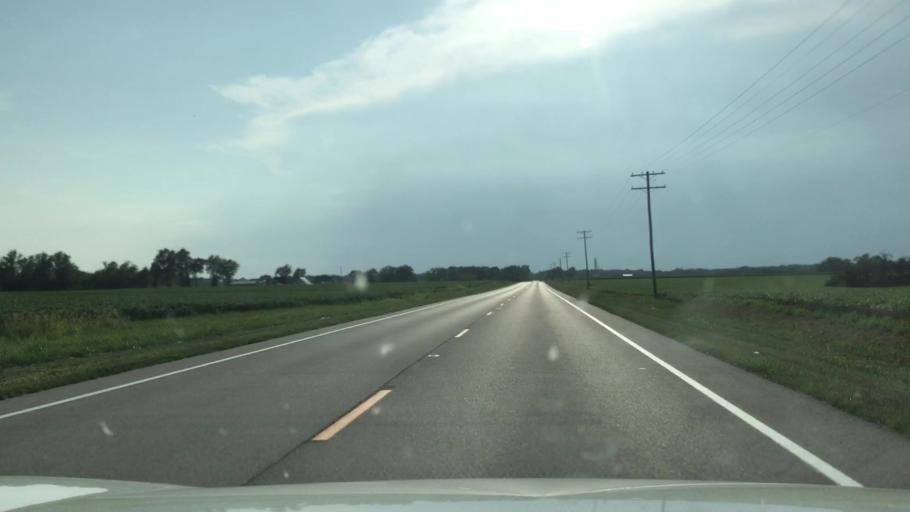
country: US
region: Illinois
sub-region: Washington County
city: Nashville
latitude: 38.4416
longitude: -89.3895
